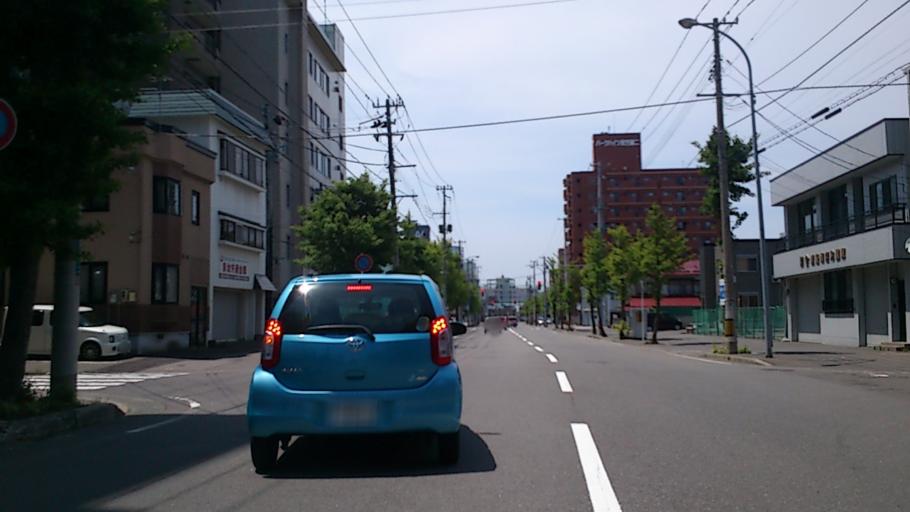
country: JP
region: Aomori
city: Aomori Shi
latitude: 40.8279
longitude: 140.7437
